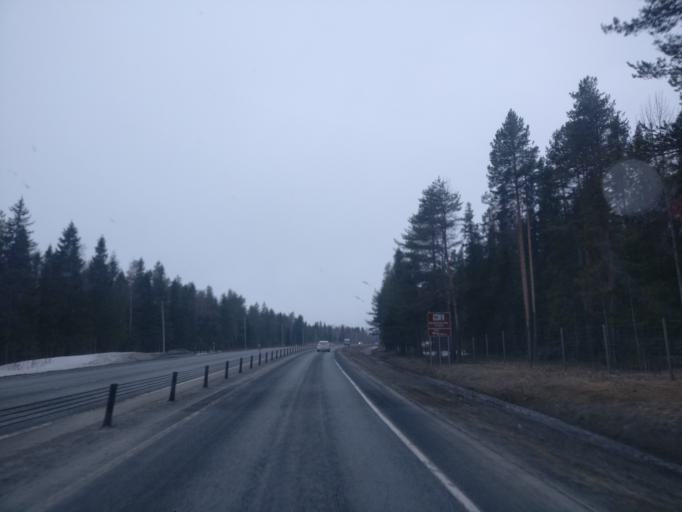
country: FI
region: Lapland
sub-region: Kemi-Tornio
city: Simo
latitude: 65.6685
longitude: 24.9418
